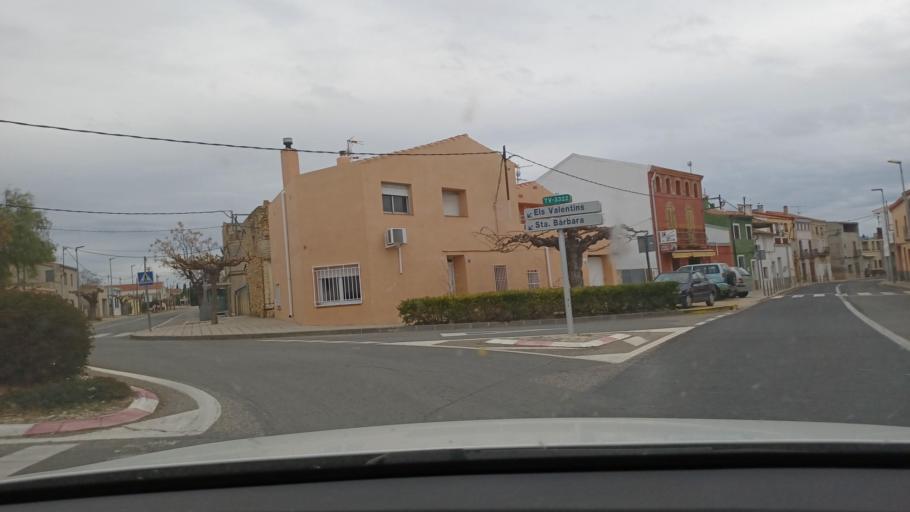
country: ES
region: Catalonia
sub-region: Provincia de Tarragona
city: Ulldecona
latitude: 40.6086
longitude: 0.3478
